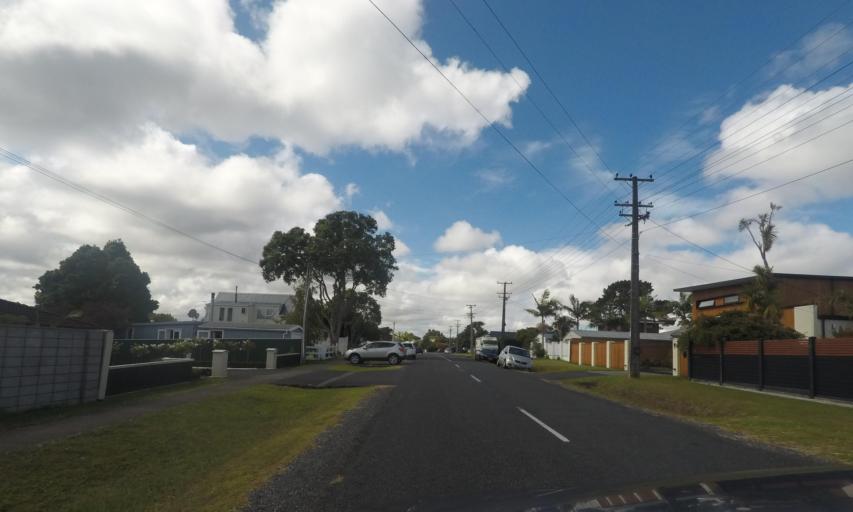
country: NZ
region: Auckland
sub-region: Auckland
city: North Shore
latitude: -36.7795
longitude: 174.6595
